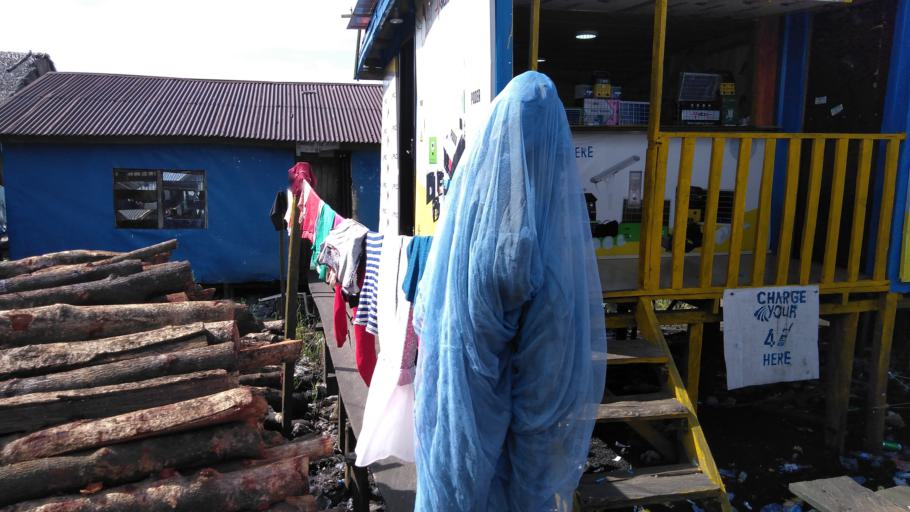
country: NG
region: Ondo
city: Igbekebo
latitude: 5.9203
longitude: 4.9676
